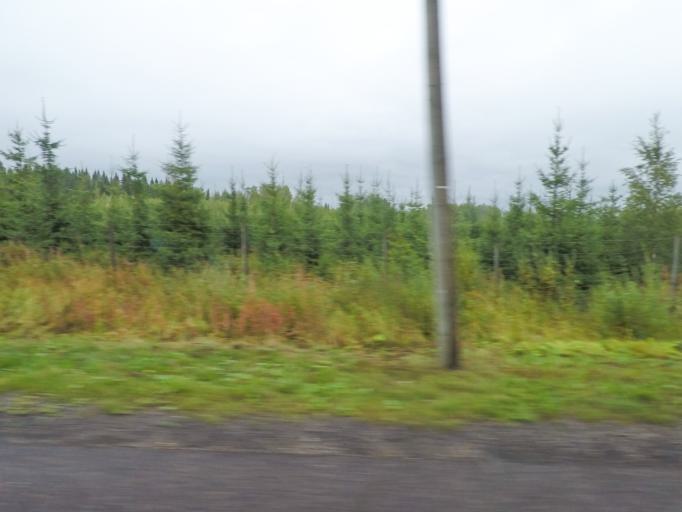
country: FI
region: Northern Savo
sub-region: Varkaus
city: Varkaus
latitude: 62.2710
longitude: 27.8648
